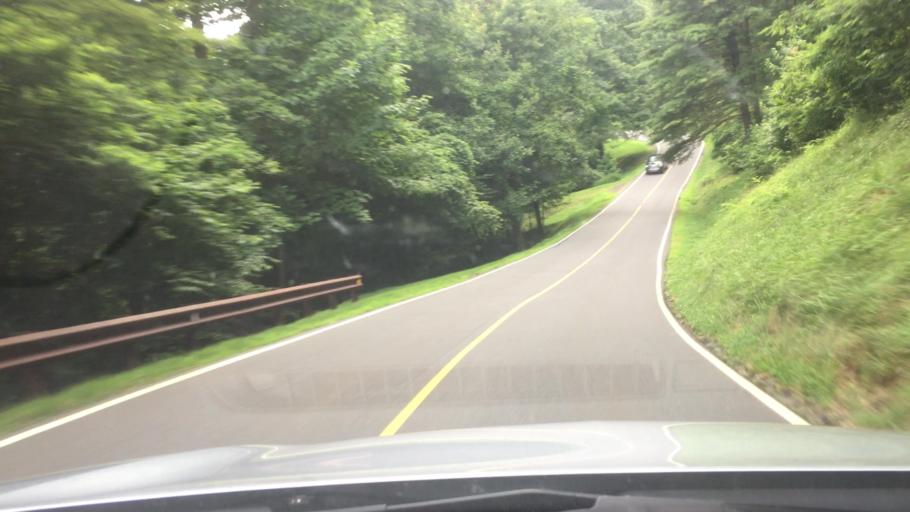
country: US
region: North Carolina
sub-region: Yancey County
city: Burnsville
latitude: 35.8873
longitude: -82.3523
